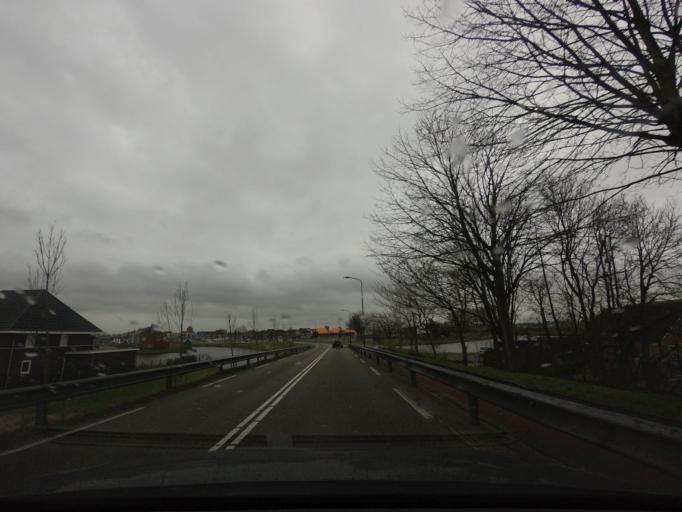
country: NL
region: North Holland
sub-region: Gemeente Langedijk
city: Broek op Langedijk
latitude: 52.6718
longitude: 4.8113
